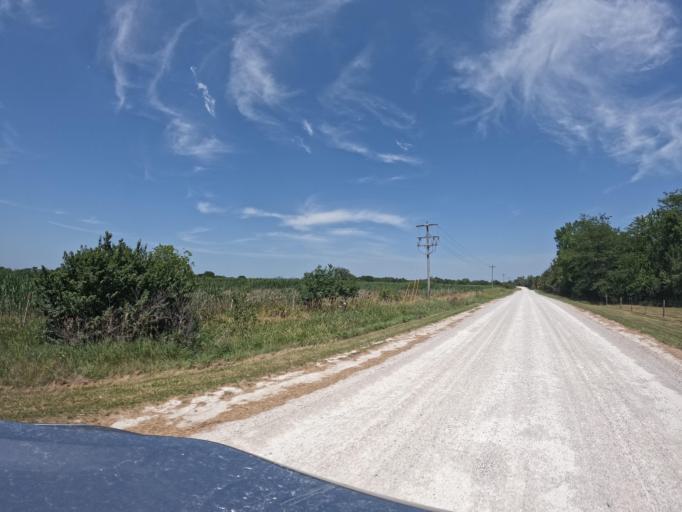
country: US
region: Iowa
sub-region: Henry County
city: Mount Pleasant
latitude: 40.9007
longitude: -91.5361
